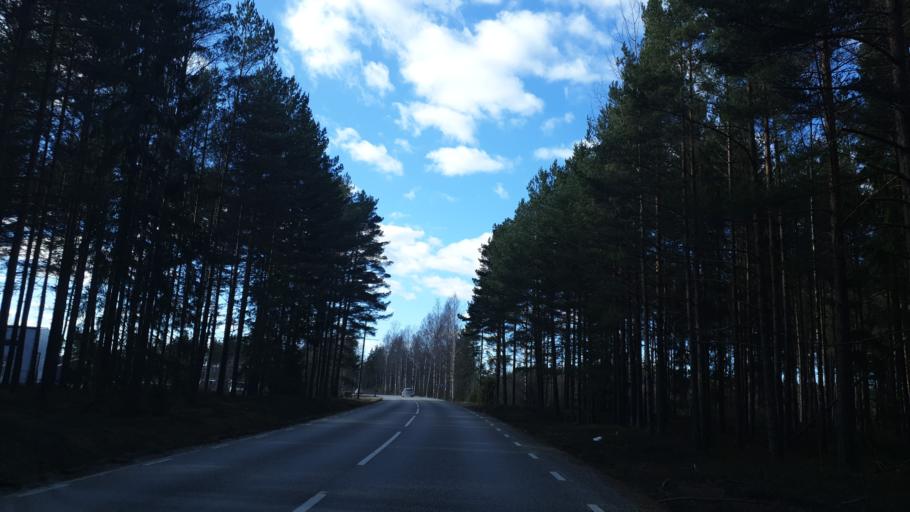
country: SE
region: OErebro
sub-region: Orebro Kommun
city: Hovsta
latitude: 59.3330
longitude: 15.1026
